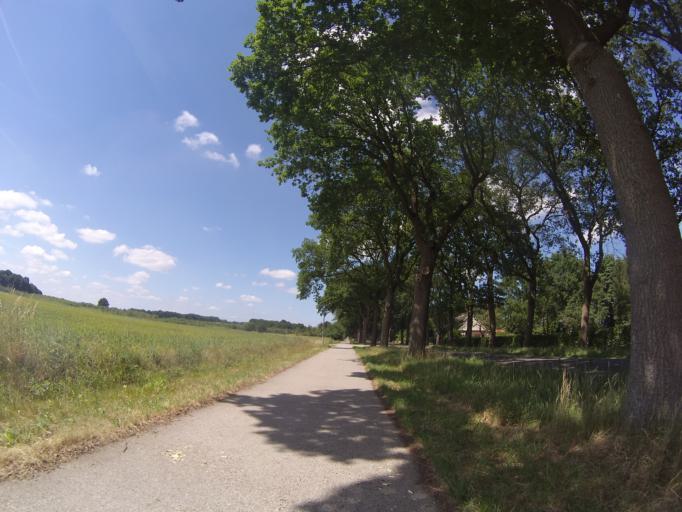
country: NL
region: Drenthe
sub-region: Gemeente Emmen
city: Emmen
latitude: 52.8449
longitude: 6.8708
